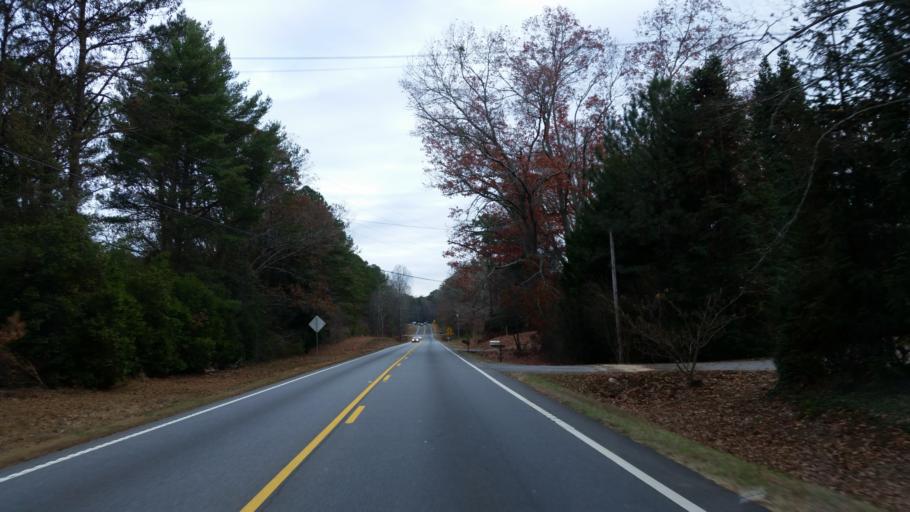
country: US
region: Georgia
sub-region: Cherokee County
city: Holly Springs
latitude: 34.2141
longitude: -84.5976
